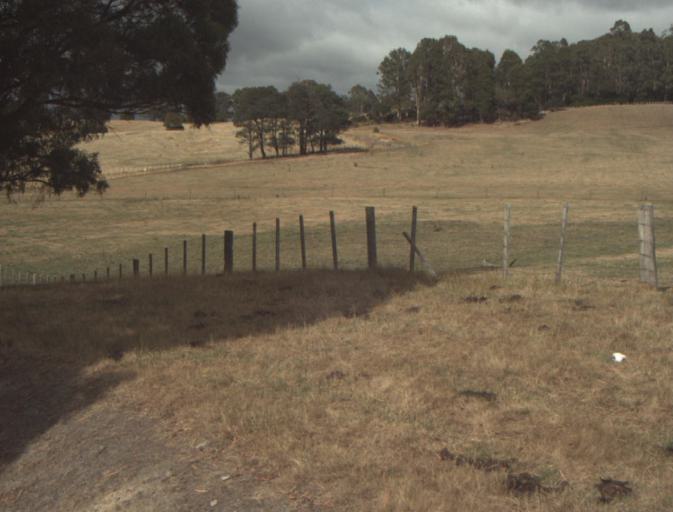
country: AU
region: Tasmania
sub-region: Dorset
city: Scottsdale
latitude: -41.4531
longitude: 147.6012
